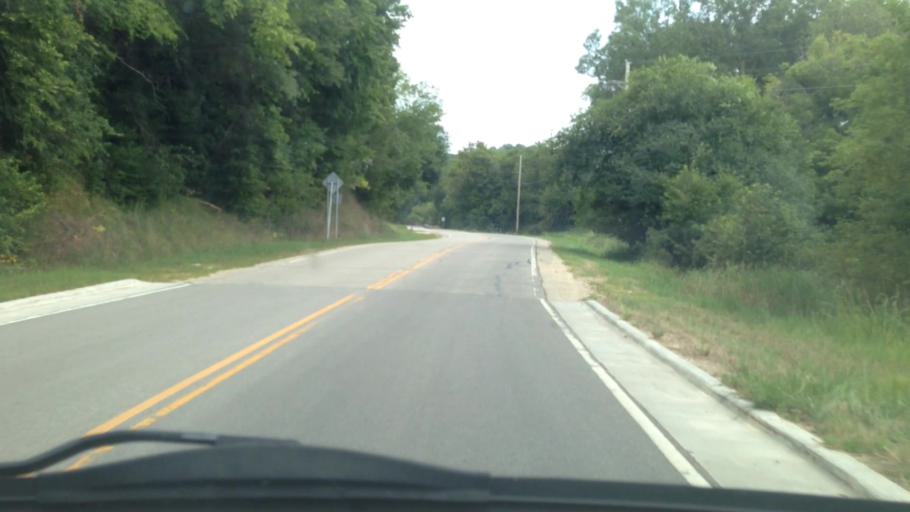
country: US
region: Minnesota
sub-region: Fillmore County
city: Preston
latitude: 43.7238
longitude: -91.9703
